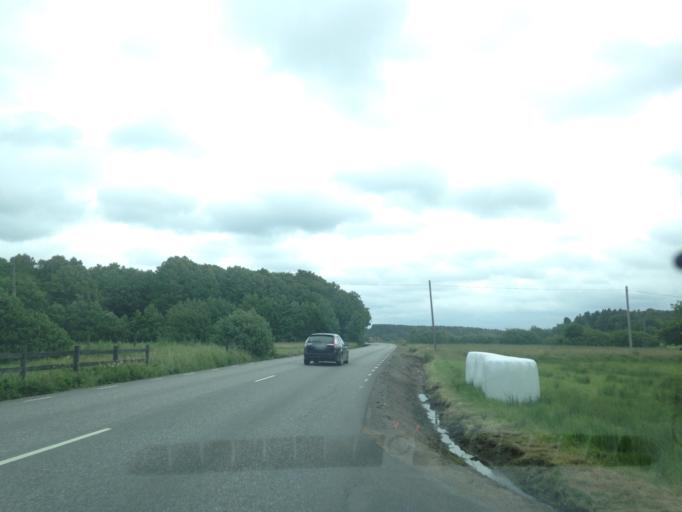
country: SE
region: Vaestra Goetaland
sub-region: Kungalvs Kommun
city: Kode
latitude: 57.8567
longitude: 11.8652
